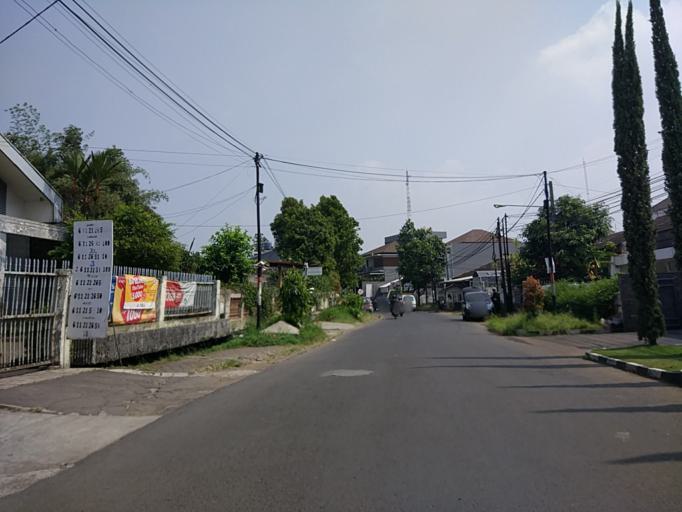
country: ID
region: West Java
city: Margahayukencana
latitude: -6.9347
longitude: 107.5753
